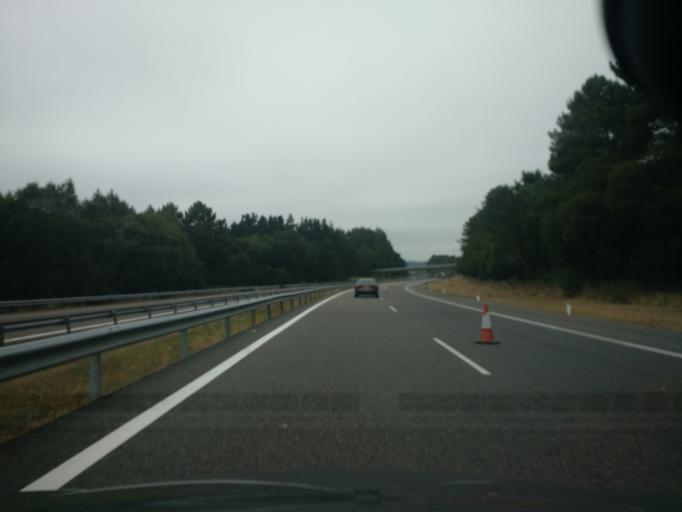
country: ES
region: Galicia
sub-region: Provincia da Coruna
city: Oroso
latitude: 42.9919
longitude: -8.4279
